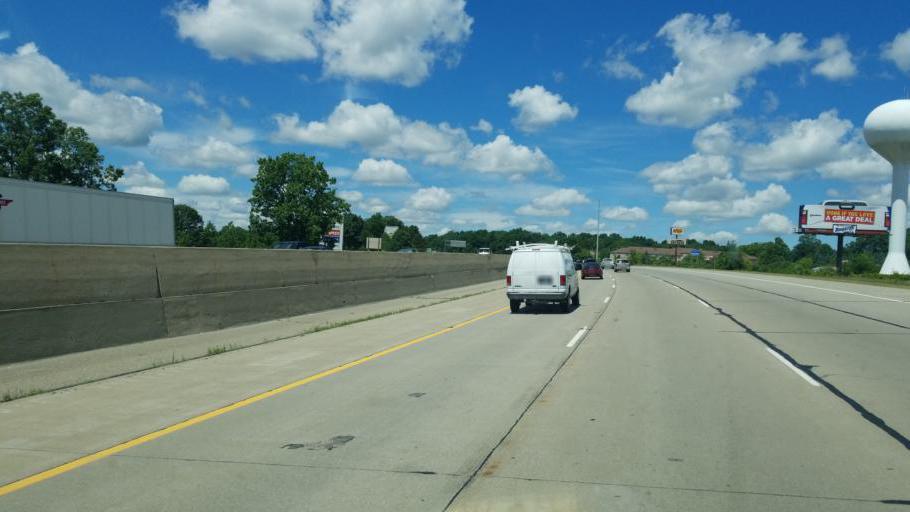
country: US
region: Michigan
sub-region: Livingston County
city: Brighton
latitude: 42.5498
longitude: -83.7922
